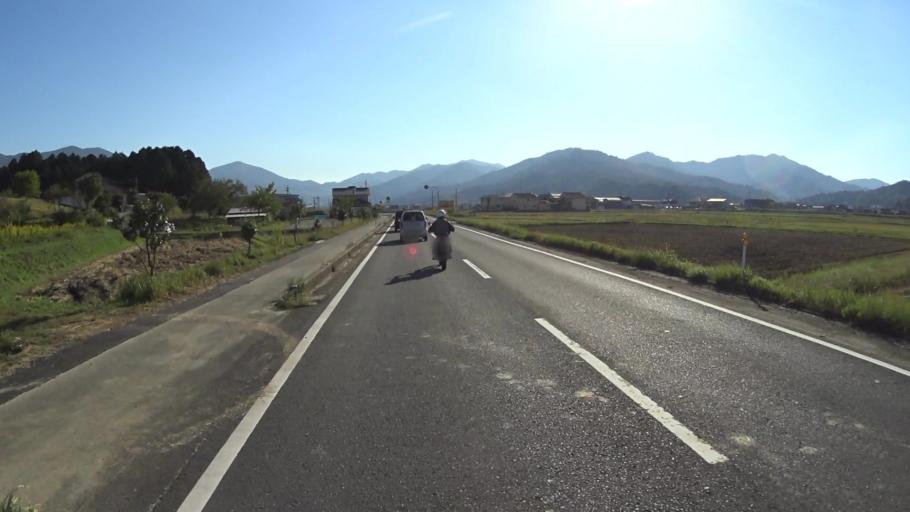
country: JP
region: Kyoto
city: Miyazu
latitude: 35.5098
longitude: 135.1045
